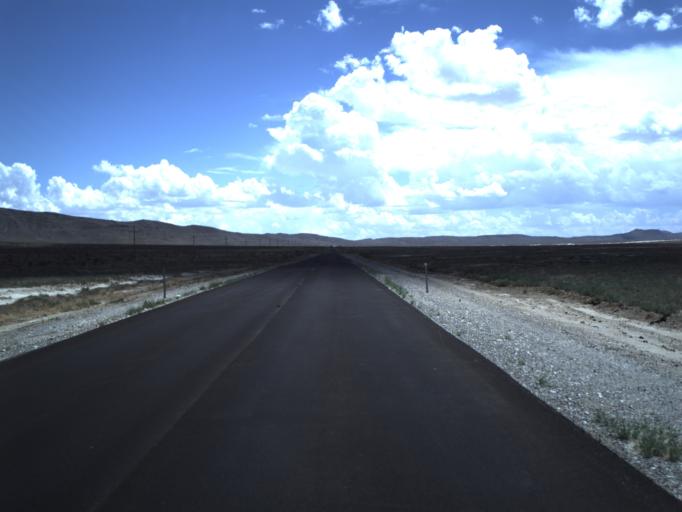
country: US
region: Utah
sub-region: Beaver County
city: Milford
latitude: 39.0494
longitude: -113.4174
